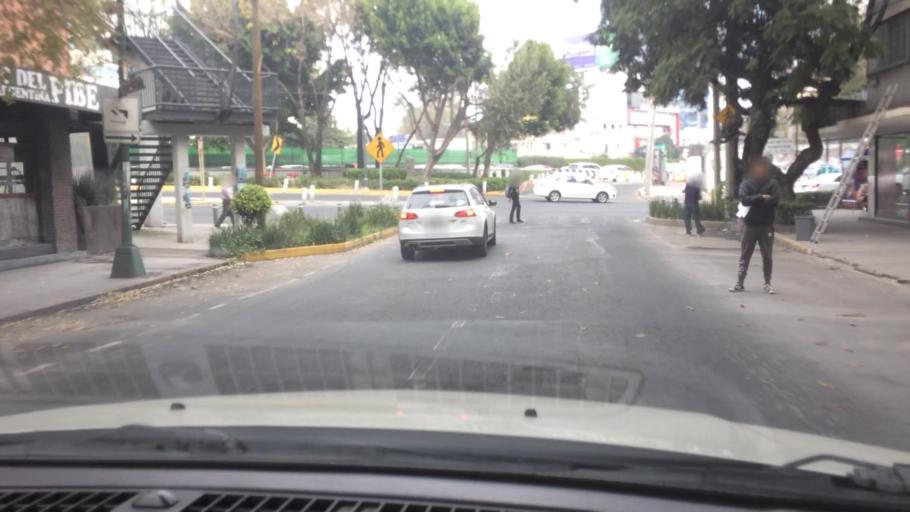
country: MX
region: Mexico City
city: Benito Juarez
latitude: 19.3984
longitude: -99.1726
